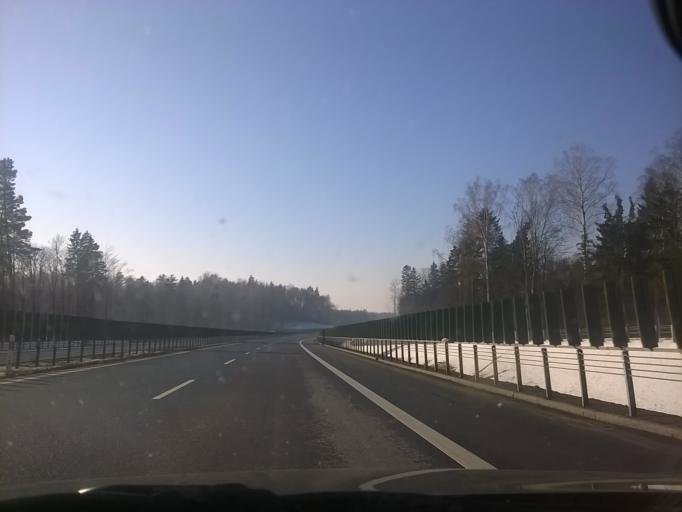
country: PL
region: Warmian-Masurian Voivodeship
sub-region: Powiat olsztynski
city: Biskupiec
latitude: 53.8330
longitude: 21.0851
